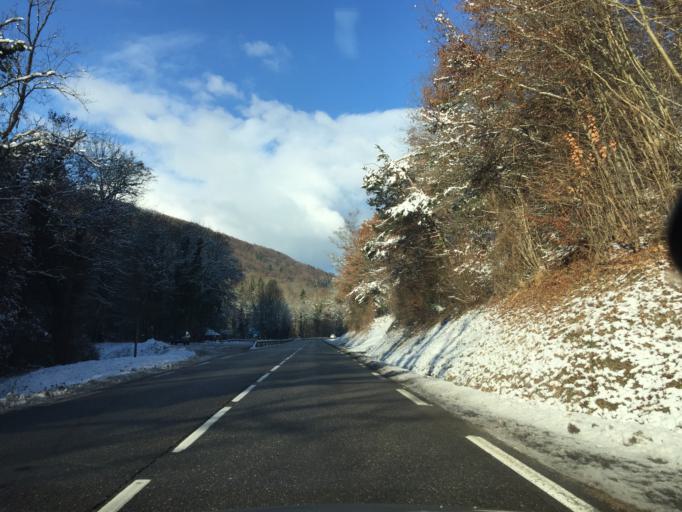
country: FR
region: Rhone-Alpes
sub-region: Departement de la Haute-Savoie
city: Armoy
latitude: 46.3524
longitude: 6.5302
